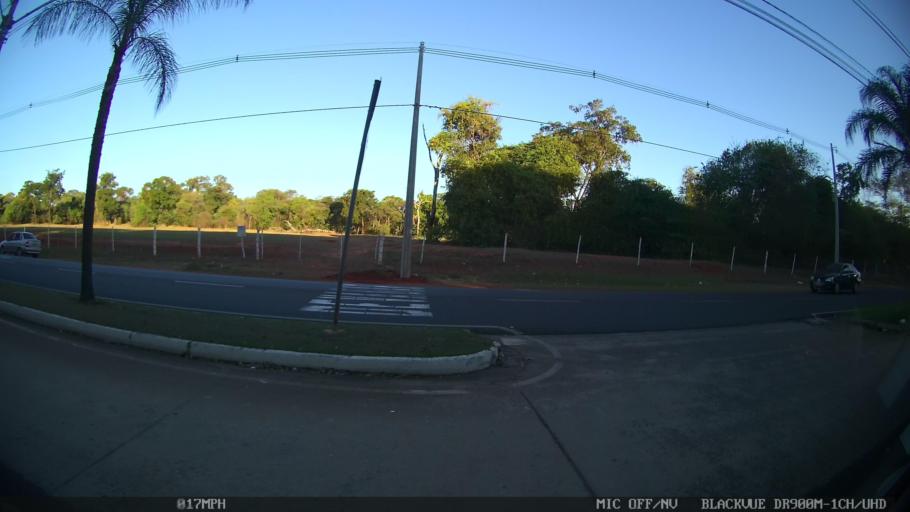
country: BR
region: Sao Paulo
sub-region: Sao Jose Do Rio Preto
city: Sao Jose do Rio Preto
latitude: -20.7659
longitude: -49.3532
